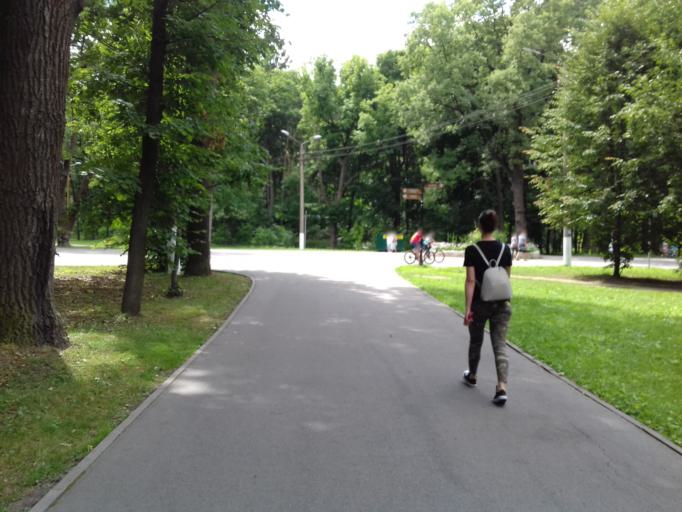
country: RU
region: Tula
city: Tula
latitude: 54.1852
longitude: 37.5868
